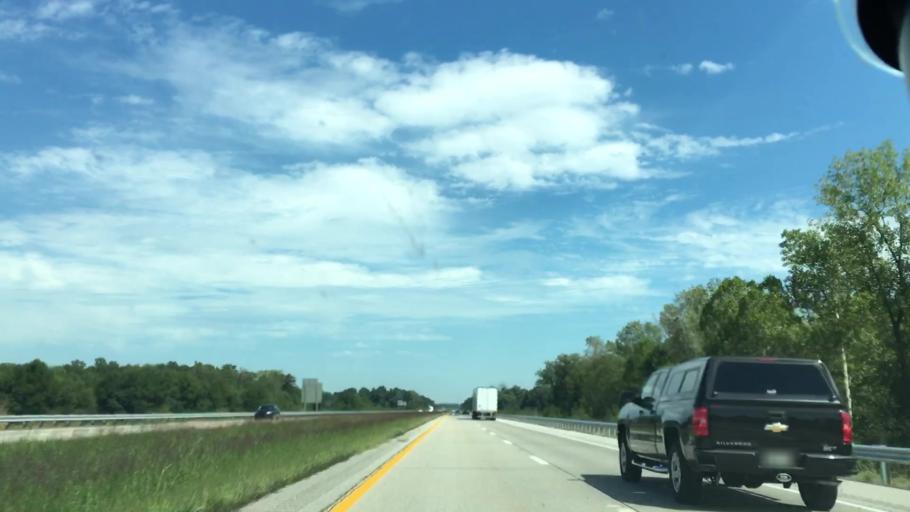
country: US
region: Kentucky
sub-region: Daviess County
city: Owensboro
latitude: 37.7585
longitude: -87.2517
